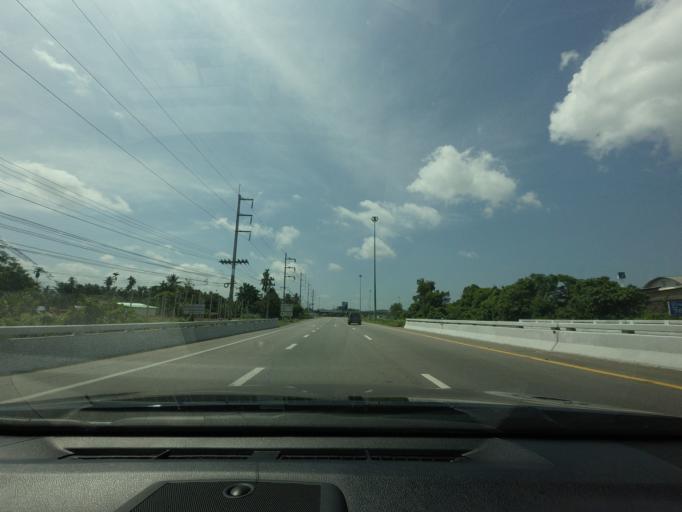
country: TH
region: Chumphon
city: Chumphon
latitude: 10.5075
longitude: 99.1167
